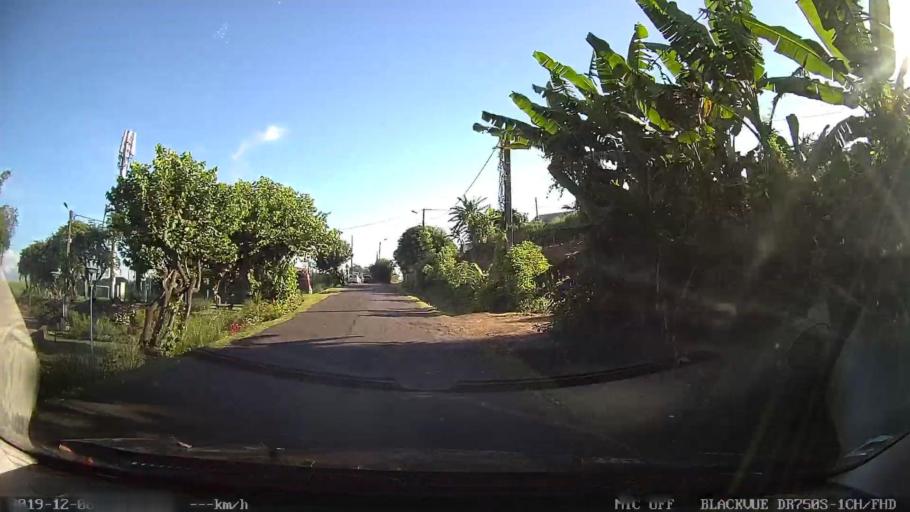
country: RE
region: Reunion
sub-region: Reunion
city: Sainte-Marie
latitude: -20.9125
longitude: 55.5289
